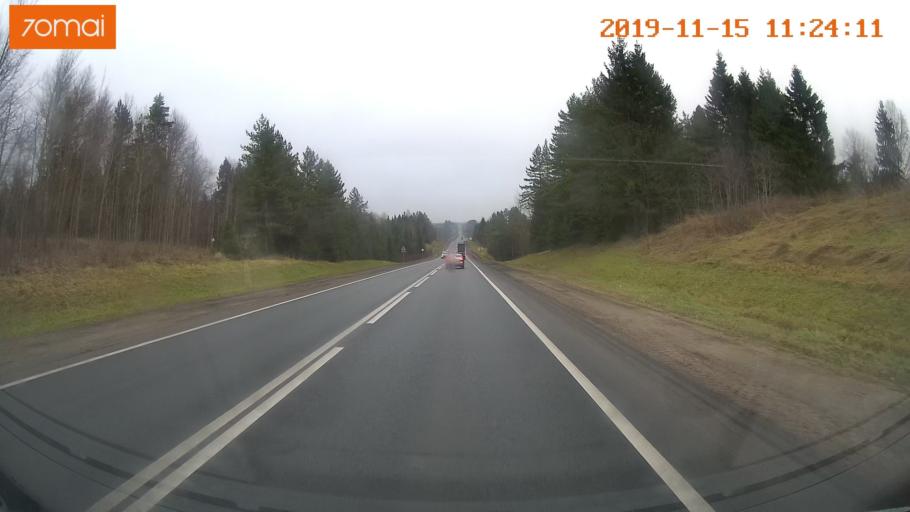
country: RU
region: Vologda
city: Molochnoye
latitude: 59.1559
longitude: 39.3998
